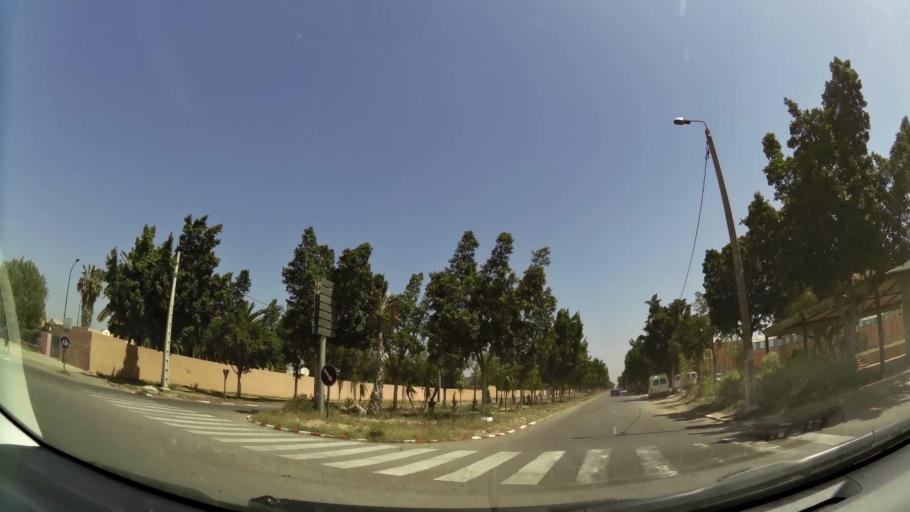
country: MA
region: Souss-Massa-Draa
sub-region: Inezgane-Ait Mellou
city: Inezgane
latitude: 30.3329
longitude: -9.4902
